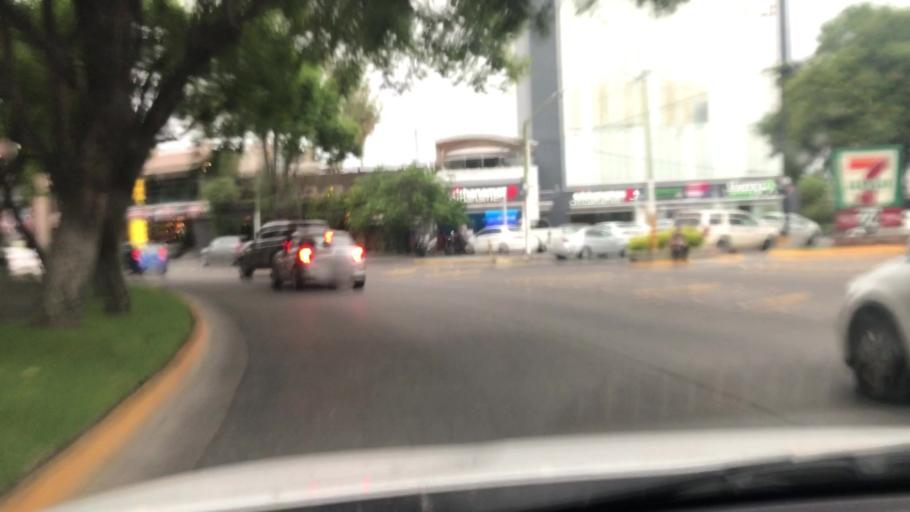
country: MX
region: Jalisco
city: Guadalajara
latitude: 20.6668
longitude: -103.4025
